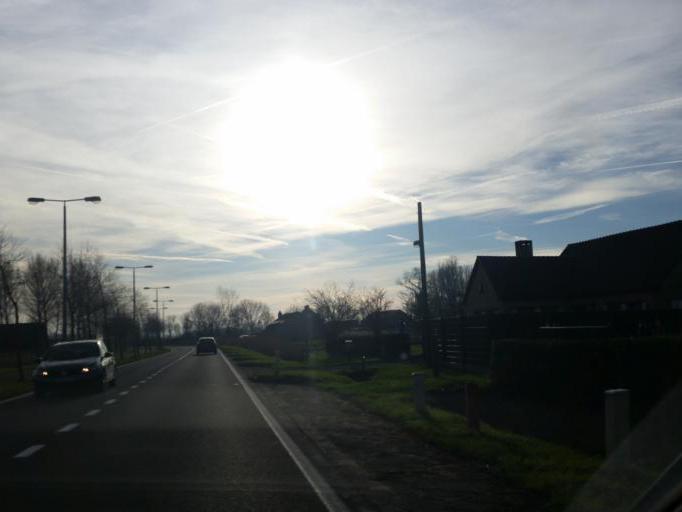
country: BE
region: Flanders
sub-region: Provincie West-Vlaanderen
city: Brugge
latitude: 51.2612
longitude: 3.2231
